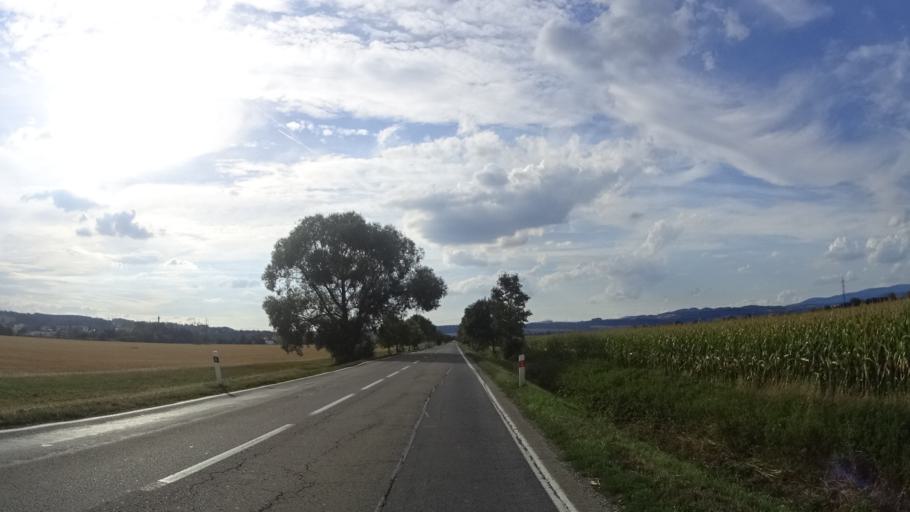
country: CZ
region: Olomoucky
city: Lestina
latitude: 49.8691
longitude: 16.9163
